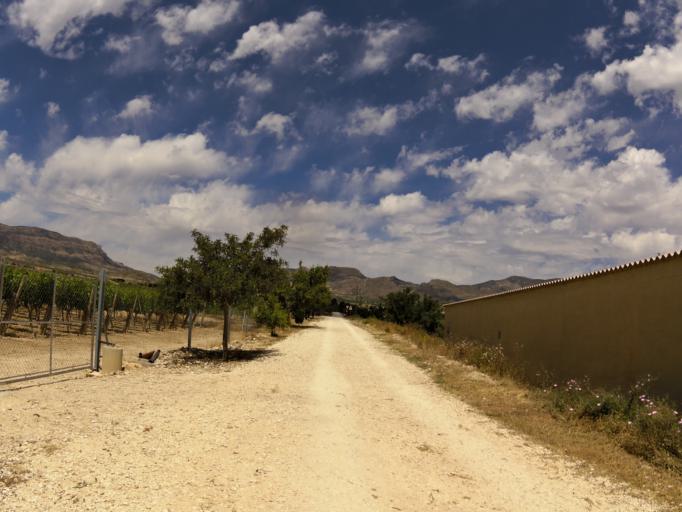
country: ES
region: Valencia
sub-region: Provincia de Alicante
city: Agost
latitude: 38.4398
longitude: -0.6496
